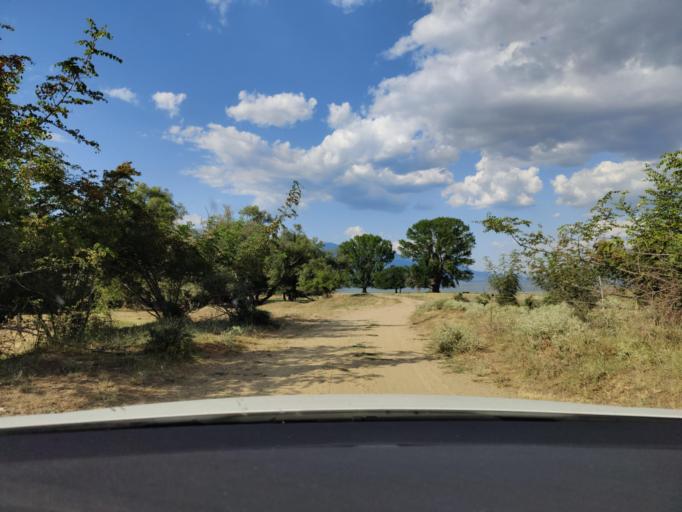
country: GR
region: Central Macedonia
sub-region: Nomos Serron
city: Chrysochorafa
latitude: 41.1864
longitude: 23.1086
